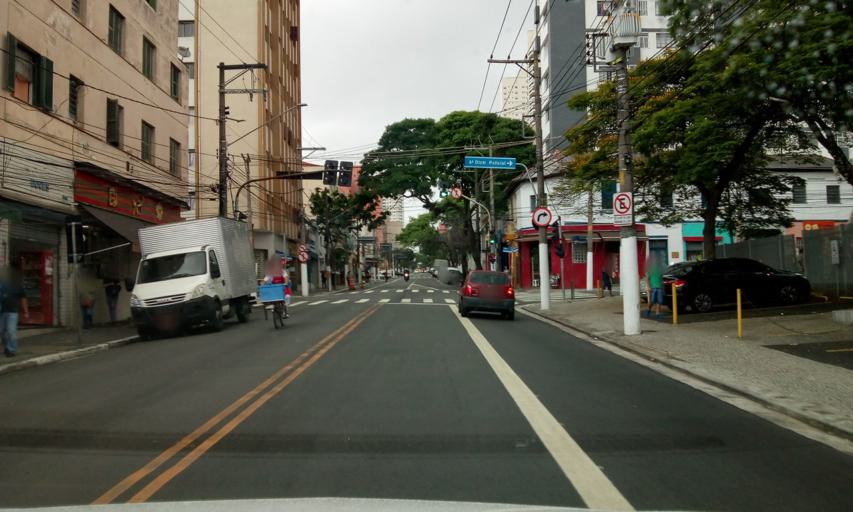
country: BR
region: Sao Paulo
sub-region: Sao Paulo
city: Sao Paulo
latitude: -23.5641
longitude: -46.6210
